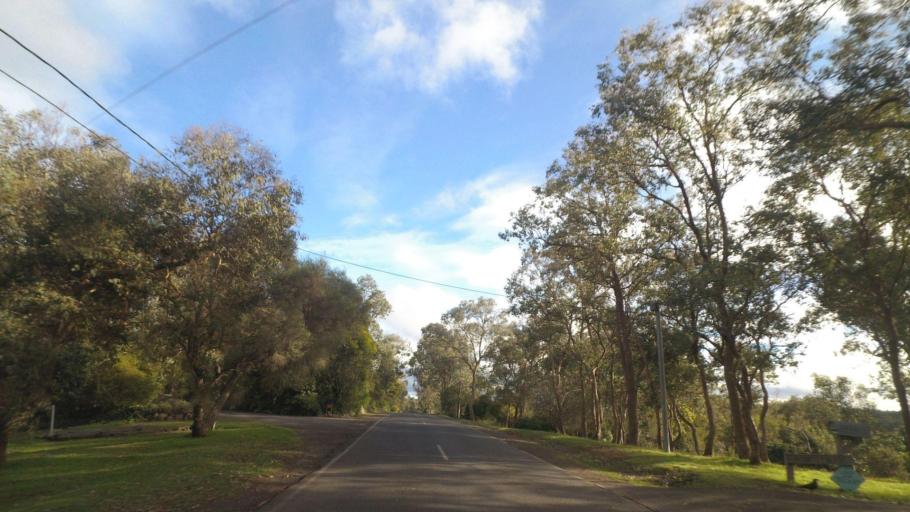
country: AU
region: Victoria
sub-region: Nillumbik
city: North Warrandyte
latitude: -37.7359
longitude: 145.2157
